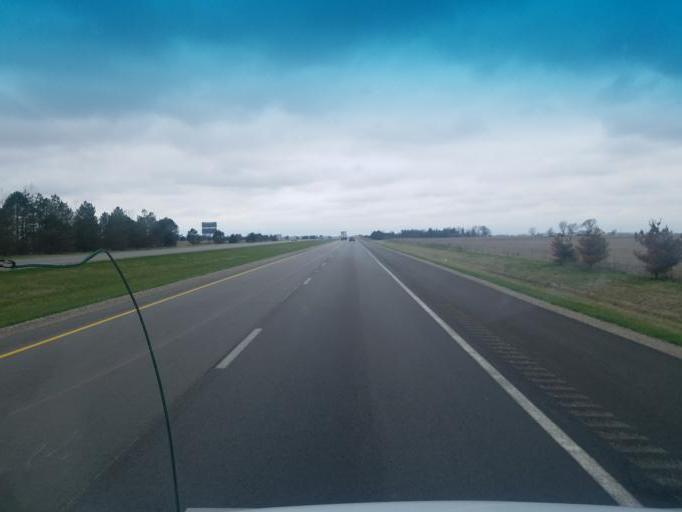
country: US
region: Ohio
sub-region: Van Wert County
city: Convoy
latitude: 40.9357
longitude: -84.7001
